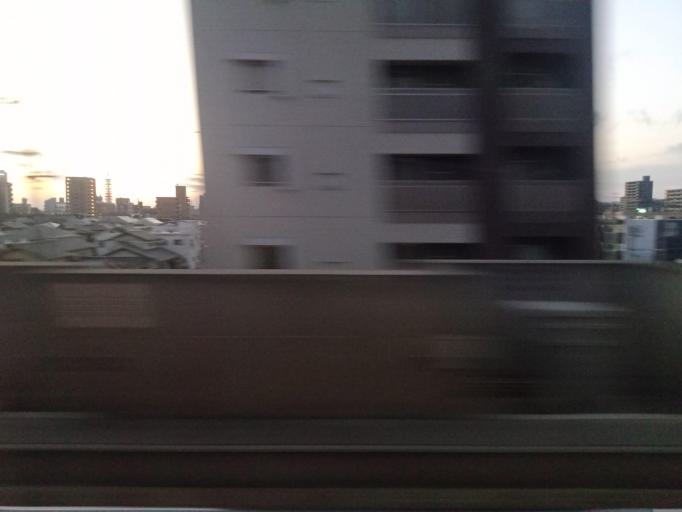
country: JP
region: Okayama
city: Okayama-shi
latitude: 34.6507
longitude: 133.9104
